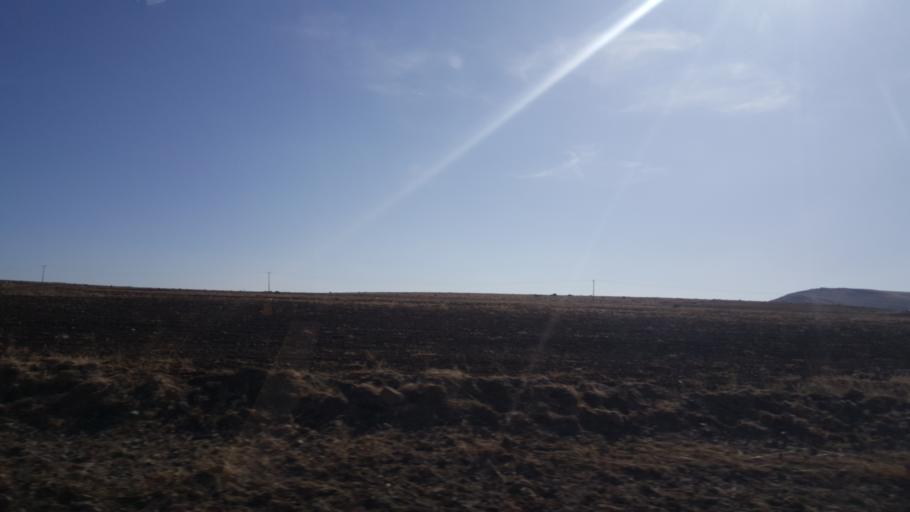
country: TR
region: Ankara
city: Altpinar
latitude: 39.2417
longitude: 32.7222
